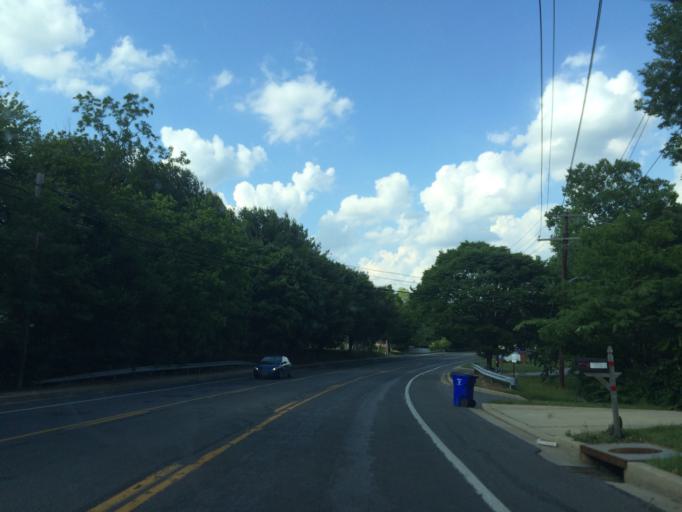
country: US
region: Maryland
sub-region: Howard County
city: Columbia
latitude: 39.2723
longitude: -76.8650
